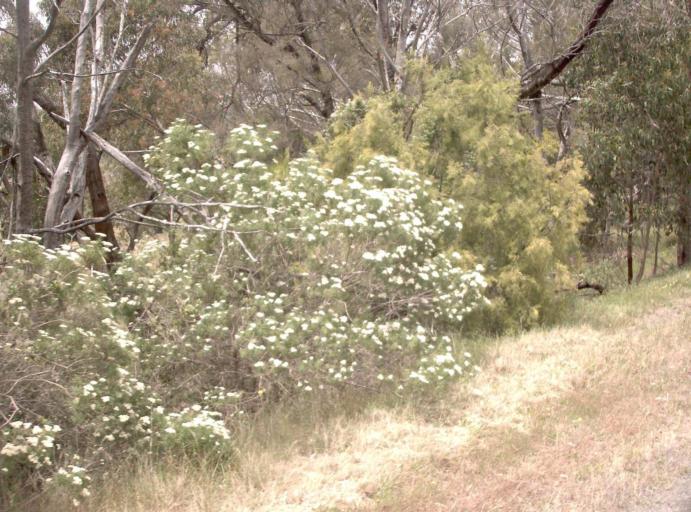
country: AU
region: Victoria
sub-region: Latrobe
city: Traralgon
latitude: -38.4509
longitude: 146.7370
